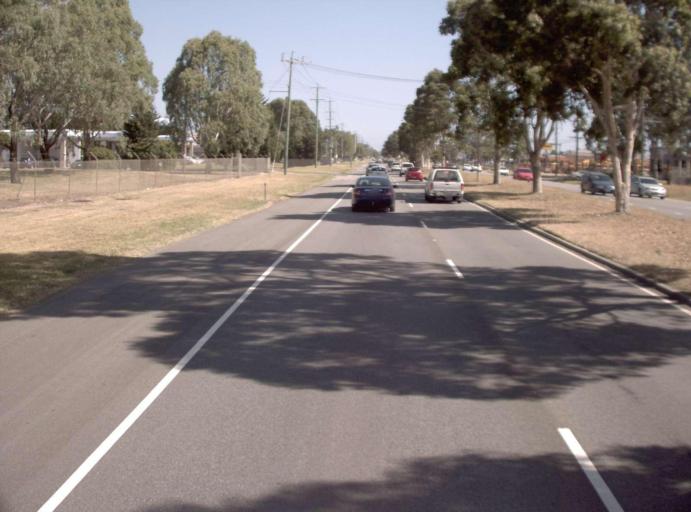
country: AU
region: Victoria
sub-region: Casey
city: Doveton
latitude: -38.0209
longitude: 145.2142
